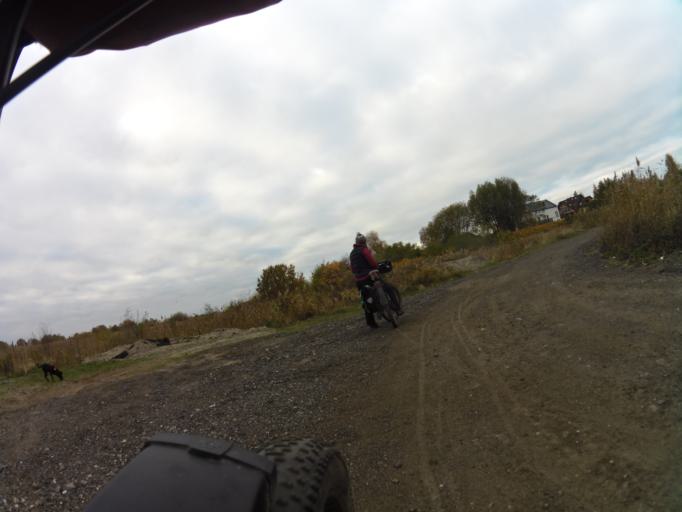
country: PL
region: Pomeranian Voivodeship
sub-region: Powiat pucki
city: Jastarnia
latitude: 54.7020
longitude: 18.6591
